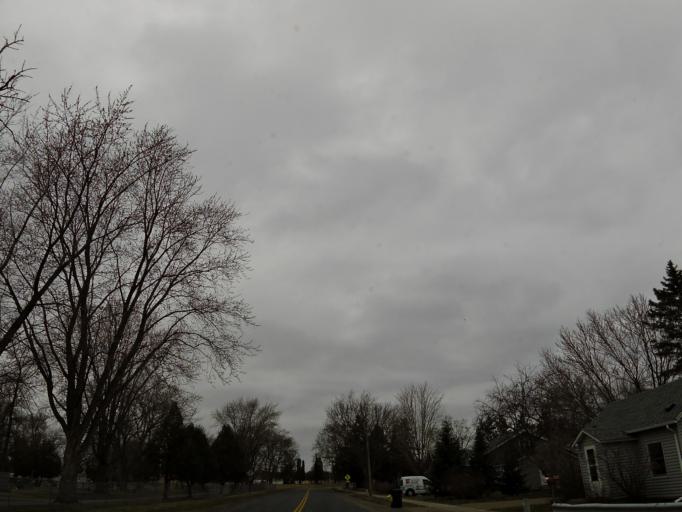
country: US
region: Minnesota
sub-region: Washington County
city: Bayport
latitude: 45.0241
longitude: -92.7846
